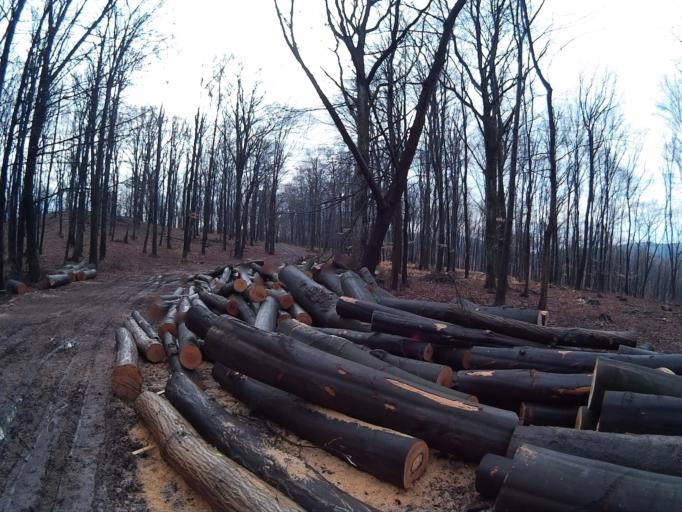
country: HU
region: Borsod-Abauj-Zemplen
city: Satoraljaujhely
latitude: 48.4222
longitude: 21.5776
